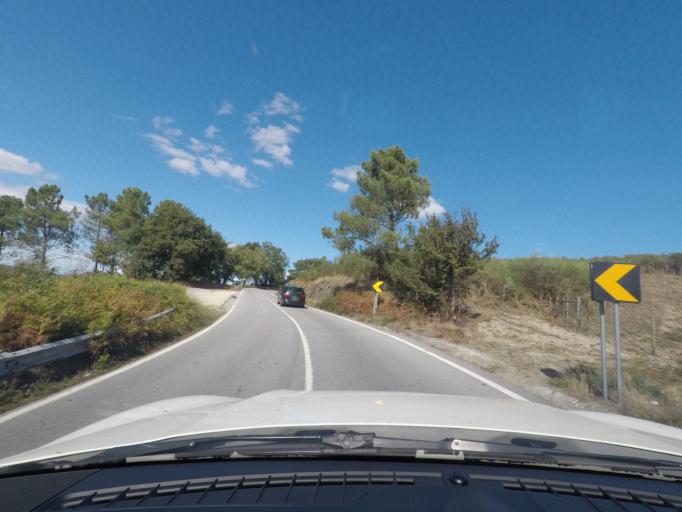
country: PT
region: Braga
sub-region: Fafe
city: Fafe
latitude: 41.4443
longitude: -8.1004
